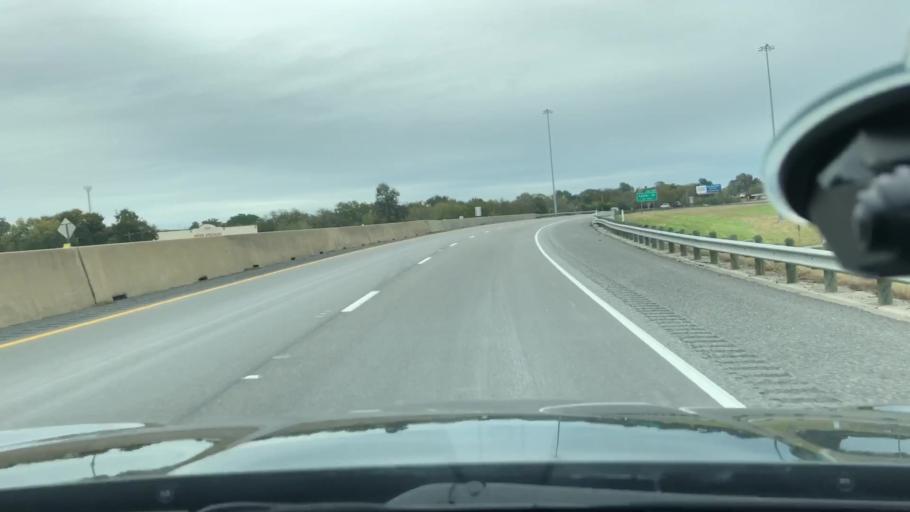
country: US
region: Texas
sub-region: Hunt County
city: Greenville
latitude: 33.1351
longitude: -96.0743
